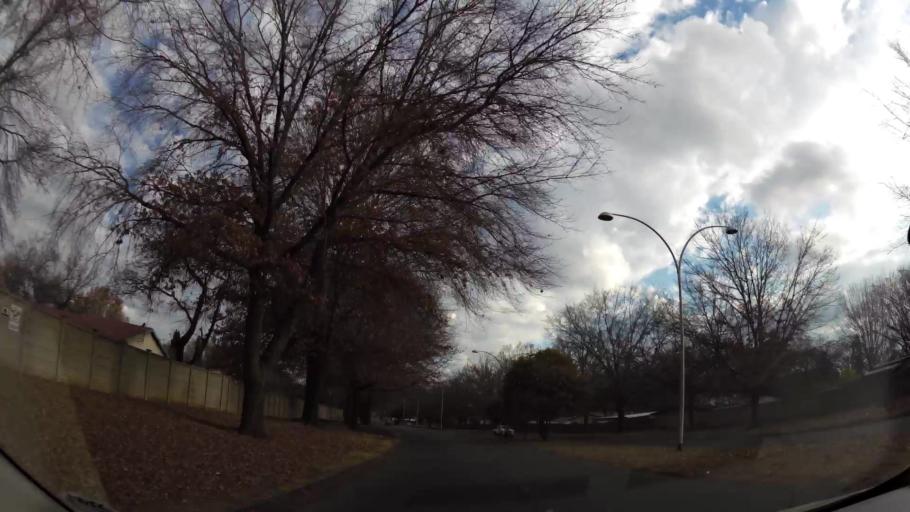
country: ZA
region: Orange Free State
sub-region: Fezile Dabi District Municipality
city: Sasolburg
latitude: -26.8001
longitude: 27.8191
